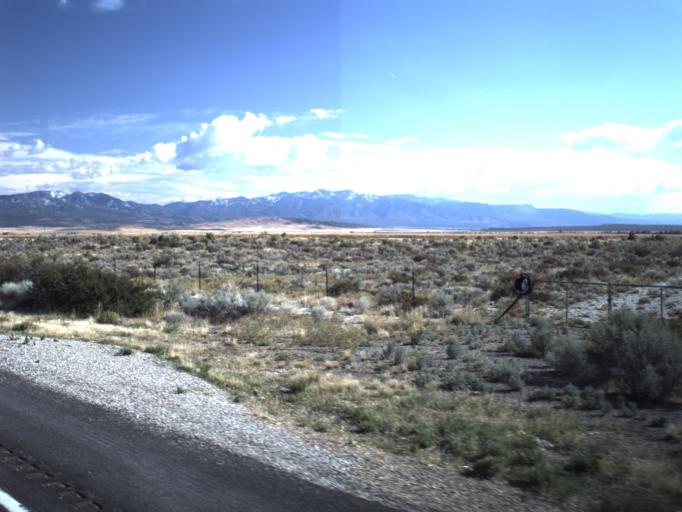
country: US
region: Utah
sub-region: Millard County
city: Fillmore
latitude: 39.1474
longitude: -112.3903
